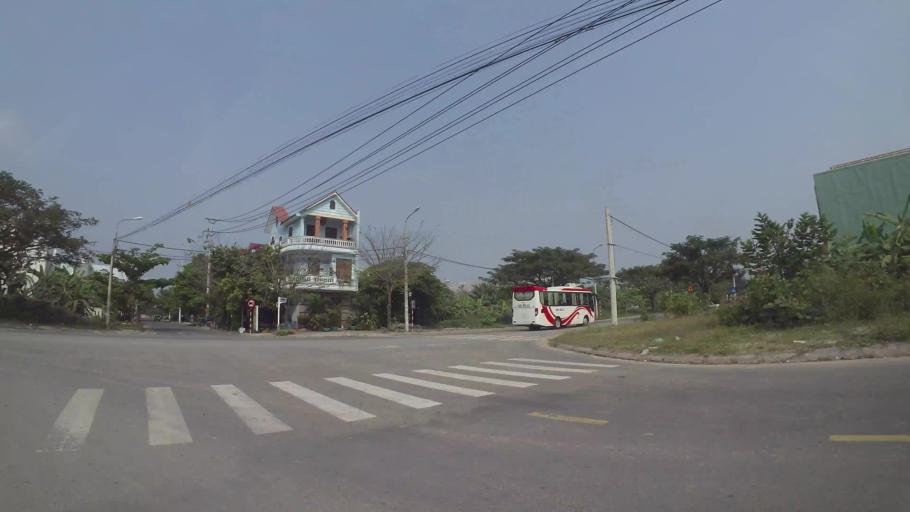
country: VN
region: Da Nang
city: Cam Le
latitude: 15.9981
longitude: 108.2163
